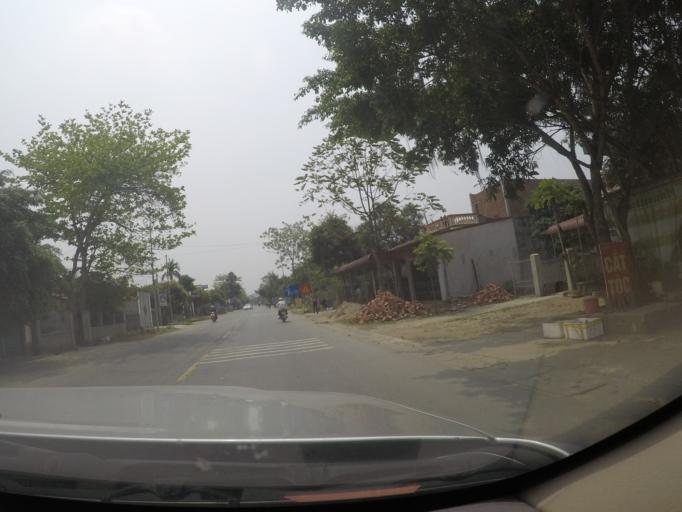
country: VN
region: Thanh Hoa
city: Thi Tran Cam Thuy
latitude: 20.2060
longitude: 105.4762
